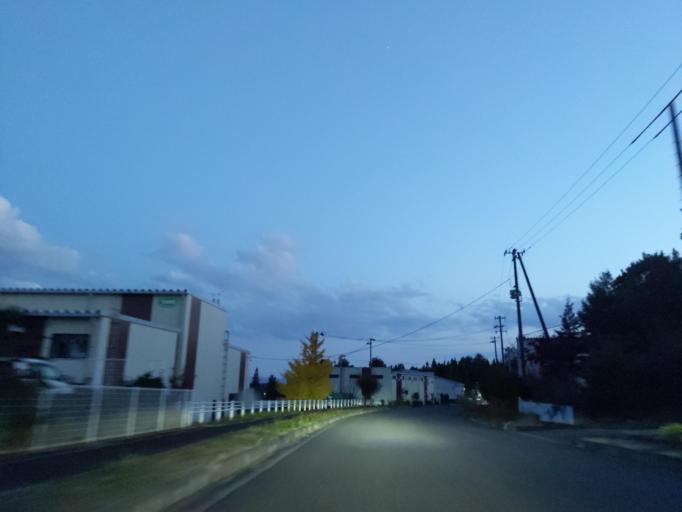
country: JP
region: Fukushima
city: Koriyama
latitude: 37.4369
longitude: 140.3076
